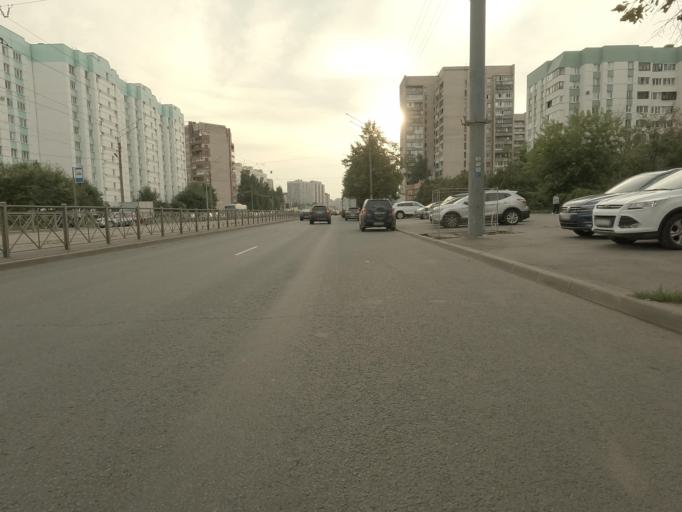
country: RU
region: St.-Petersburg
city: Dachnoye
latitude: 59.8597
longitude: 30.2395
